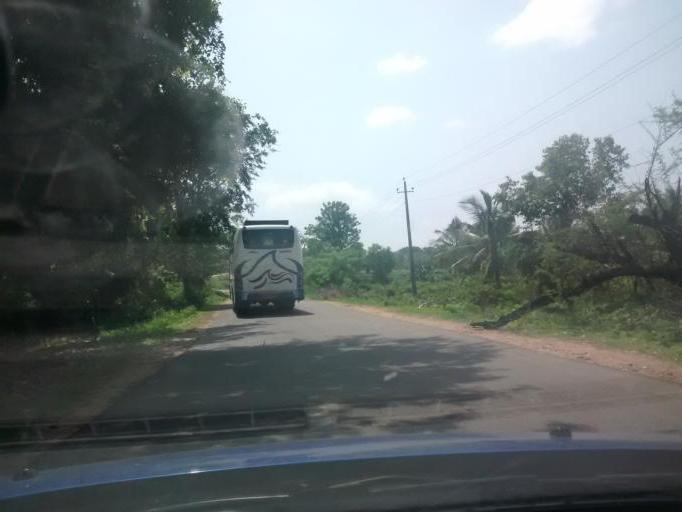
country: IN
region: Karnataka
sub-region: Hassan
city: Konanur
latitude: 12.5816
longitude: 76.1845
